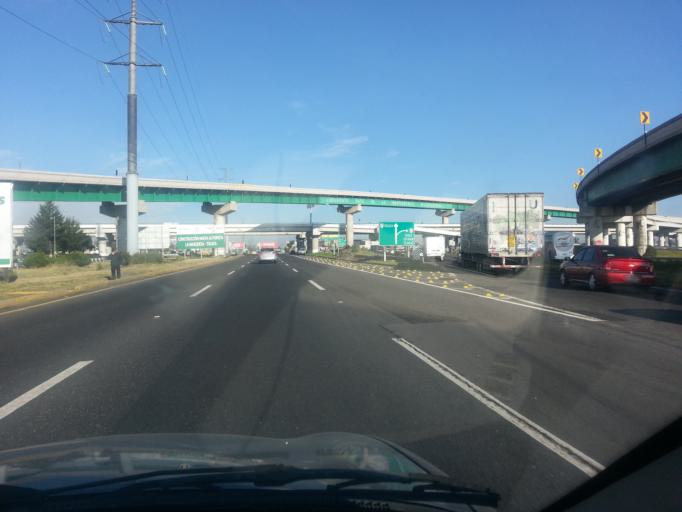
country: MX
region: Morelos
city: Lerma de Villada
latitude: 19.2829
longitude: -99.5199
